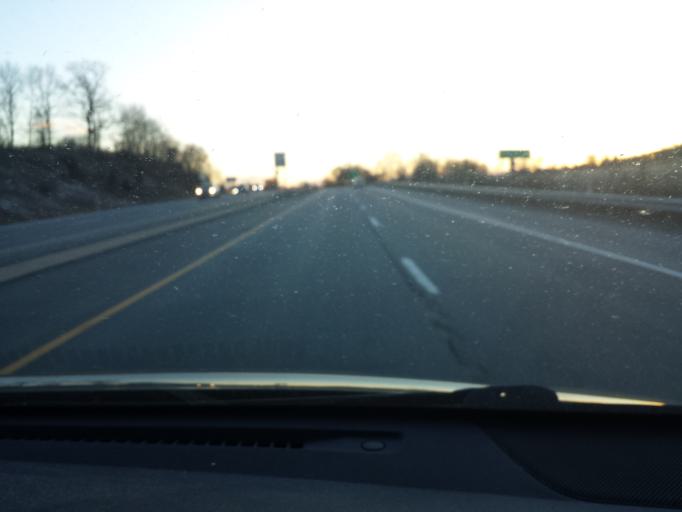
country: US
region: Pennsylvania
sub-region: Centre County
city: Bellefonte
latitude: 40.9372
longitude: -77.7323
